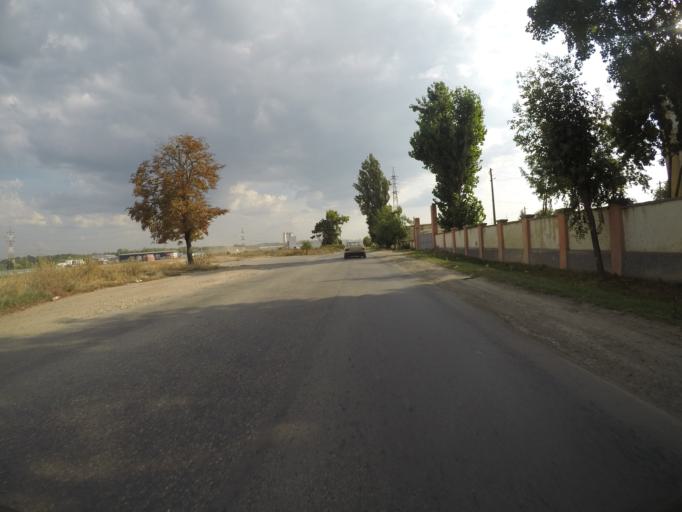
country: RO
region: Cluj
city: Turda
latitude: 46.5443
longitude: 23.7837
